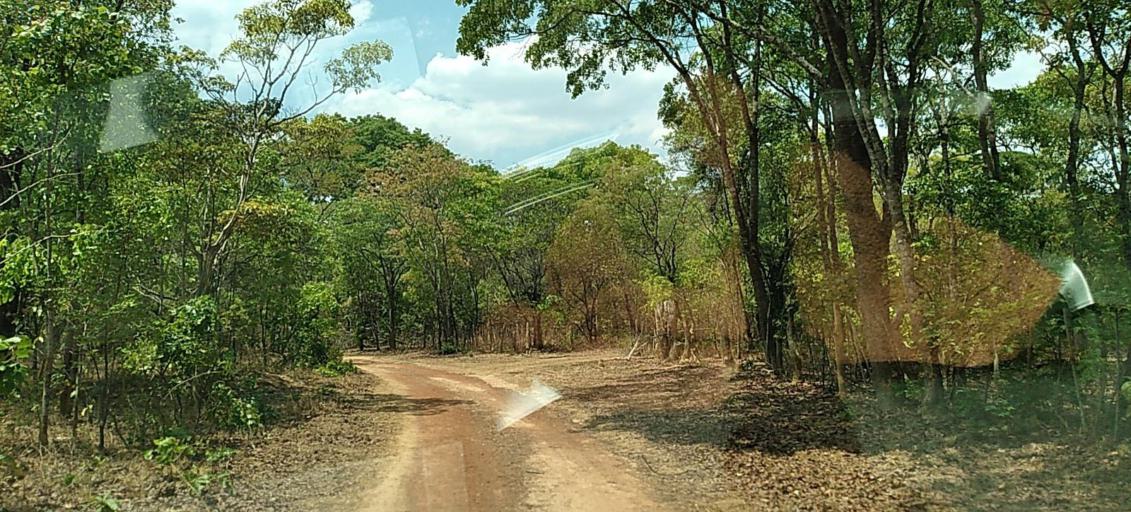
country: ZM
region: Copperbelt
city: Chililabombwe
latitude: -12.4825
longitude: 27.6432
